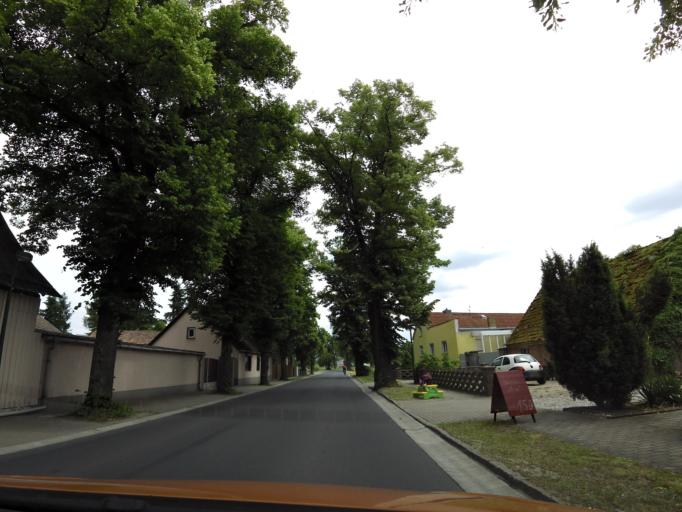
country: DE
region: Brandenburg
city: Zossen
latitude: 52.2257
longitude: 13.4160
